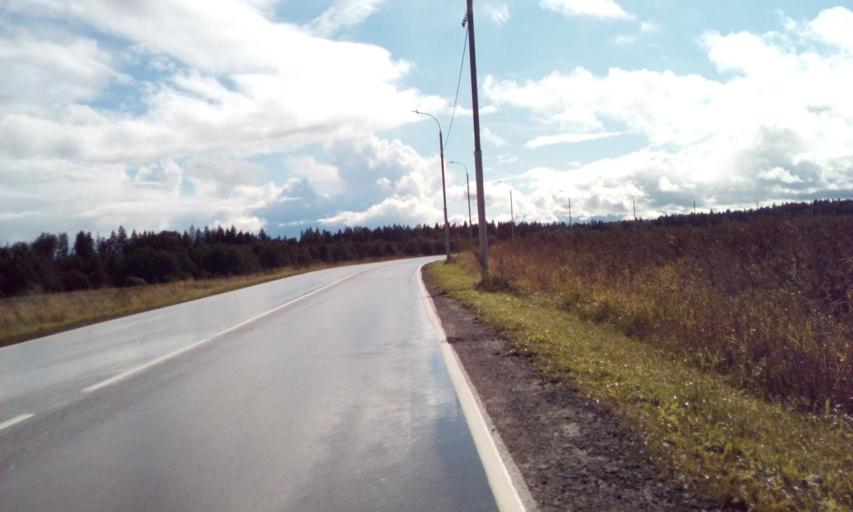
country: RU
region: Moskovskaya
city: Kievskij
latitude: 55.4447
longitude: 36.9404
